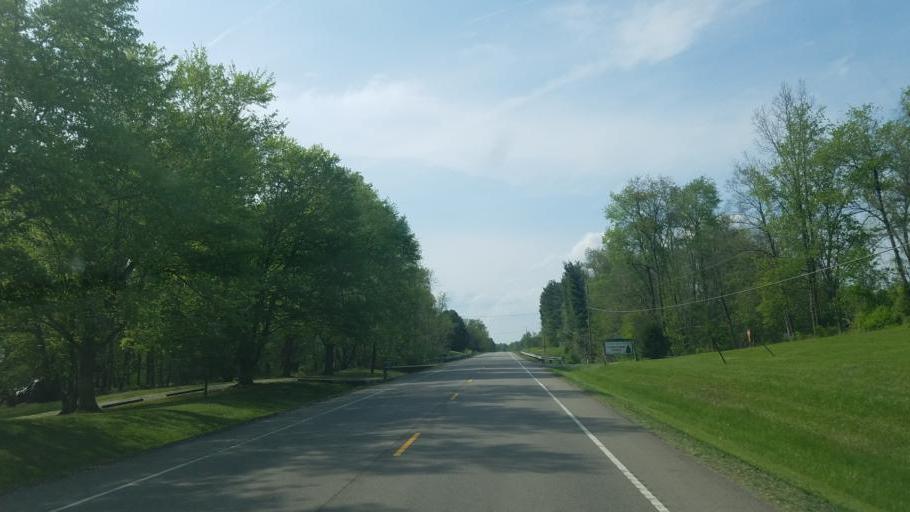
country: US
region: Ohio
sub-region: Licking County
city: Johnstown
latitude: 40.1089
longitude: -82.6433
